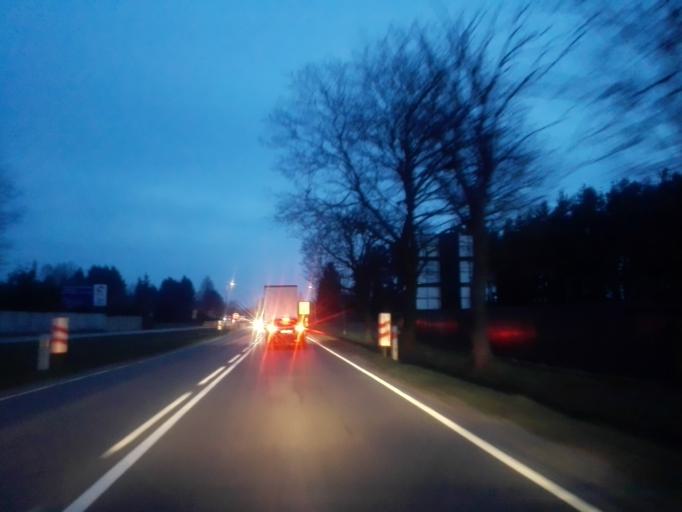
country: PL
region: Podlasie
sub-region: Lomza
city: Lomza
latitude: 53.1464
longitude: 22.0463
